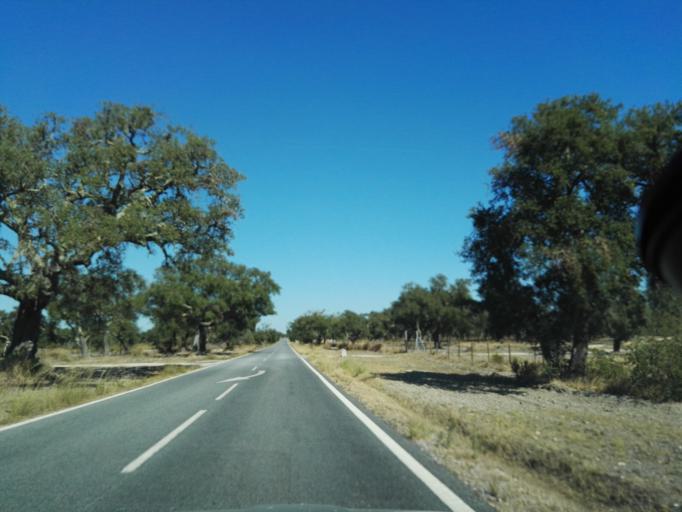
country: PT
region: Santarem
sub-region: Benavente
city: Poceirao
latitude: 38.8090
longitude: -8.7973
